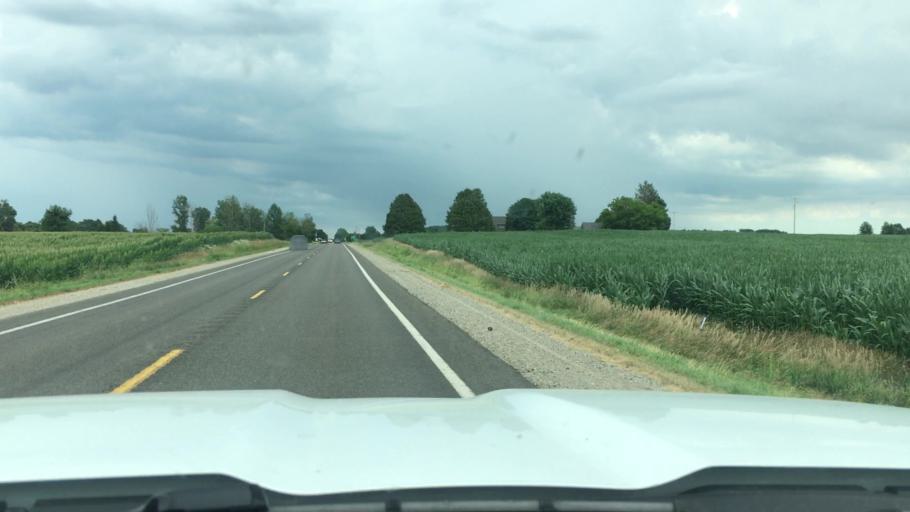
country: US
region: Michigan
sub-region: Montcalm County
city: Carson City
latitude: 43.1775
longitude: -84.9239
